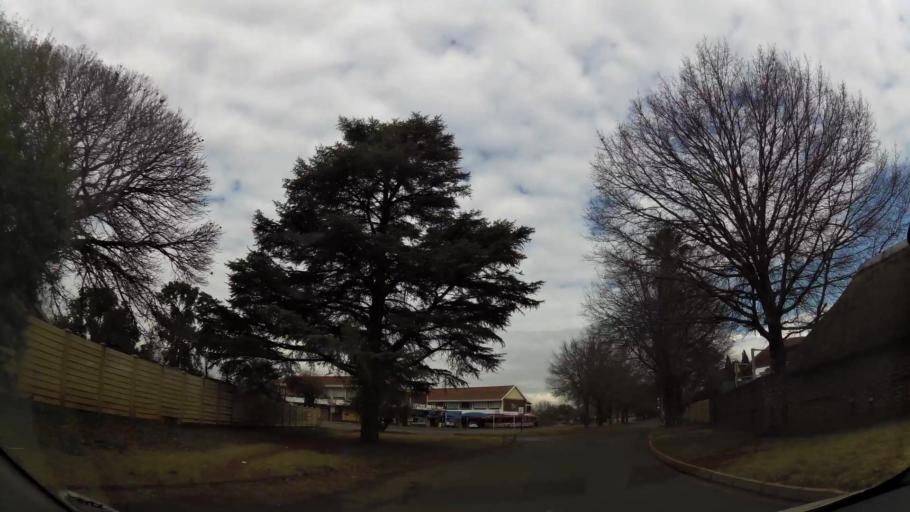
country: ZA
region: Gauteng
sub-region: Sedibeng District Municipality
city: Vereeniging
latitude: -26.6401
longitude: 27.9771
